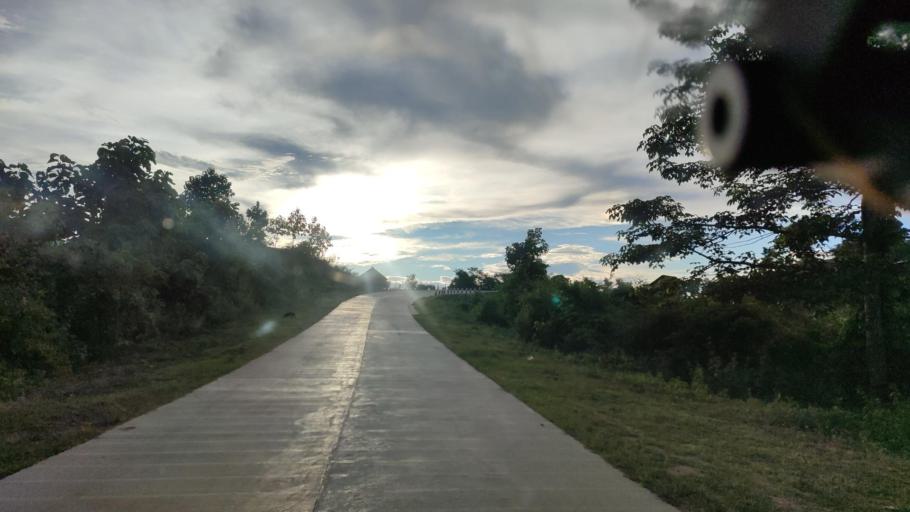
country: MM
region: Magway
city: Taungdwingyi
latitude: 20.0402
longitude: 95.7817
